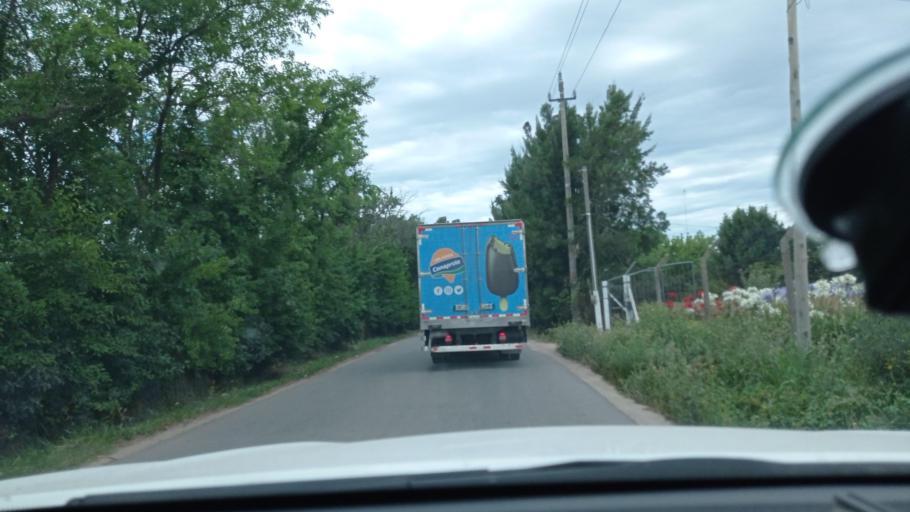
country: UY
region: Canelones
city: La Paz
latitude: -34.8111
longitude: -56.1936
